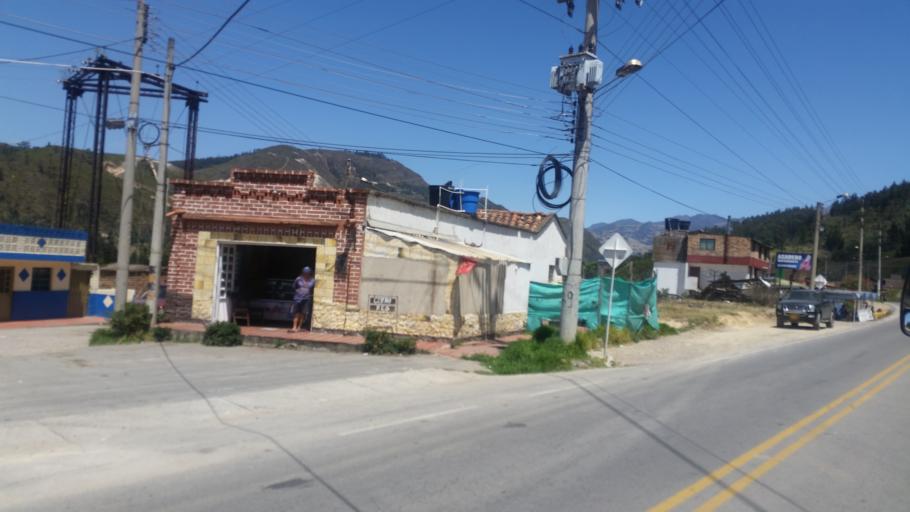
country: CO
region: Boyaca
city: Topaga
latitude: 5.7677
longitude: -72.8663
